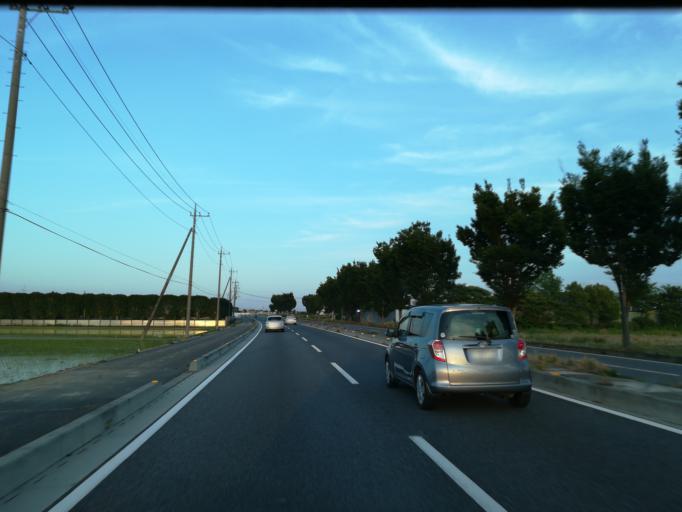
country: JP
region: Saitama
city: Hanyu
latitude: 36.1521
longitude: 139.5107
